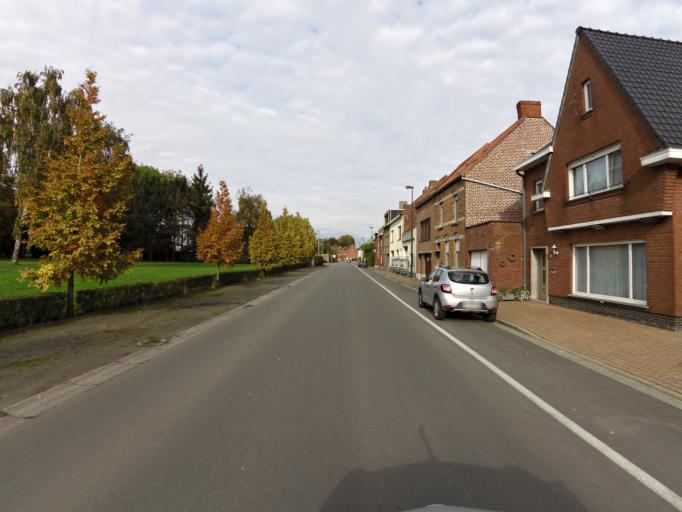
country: BE
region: Flanders
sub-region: Provincie West-Vlaanderen
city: Torhout
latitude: 51.0630
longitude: 3.1067
